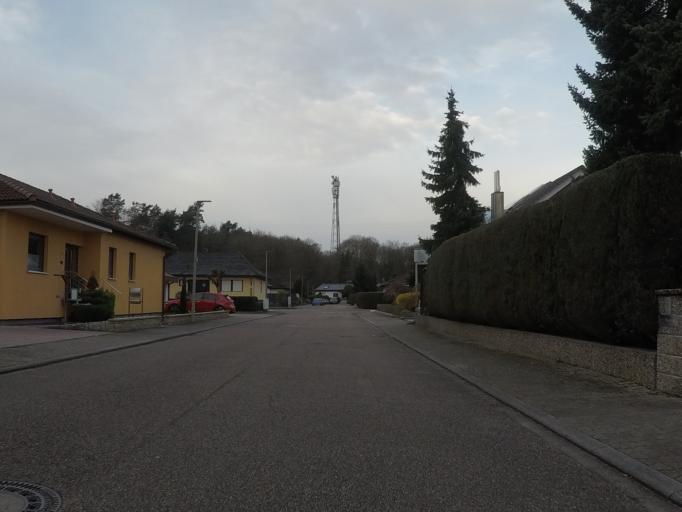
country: DE
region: Rheinland-Pfalz
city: Worth am Rhein
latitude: 49.0530
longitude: 8.2405
